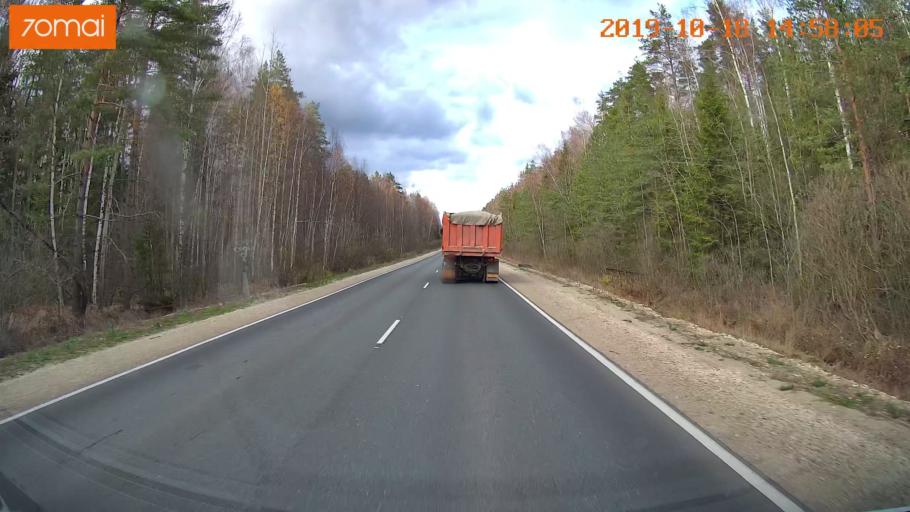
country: RU
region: Vladimir
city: Kurlovo
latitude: 55.4868
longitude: 40.5786
